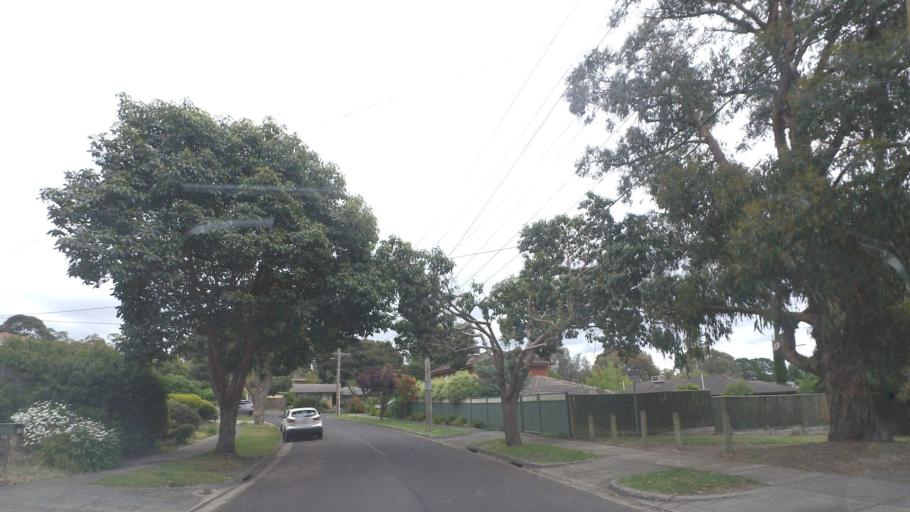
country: AU
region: Victoria
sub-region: Maroondah
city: Croydon South
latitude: -37.8025
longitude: 145.2674
